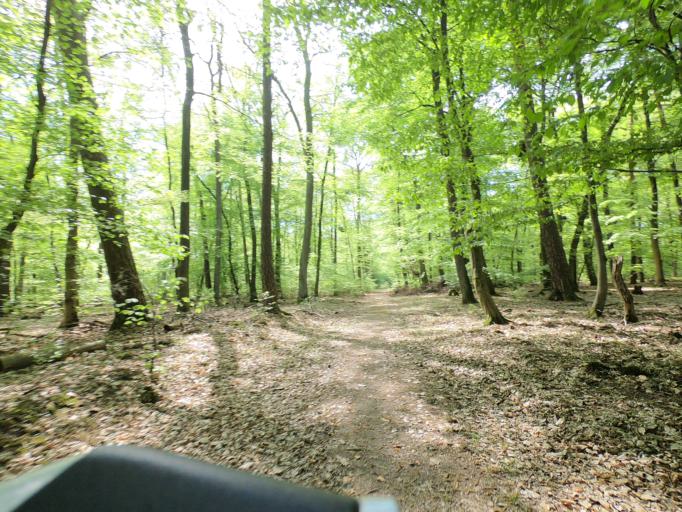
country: DE
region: Hesse
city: Morfelden-Walldorf
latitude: 50.0201
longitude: 8.5658
